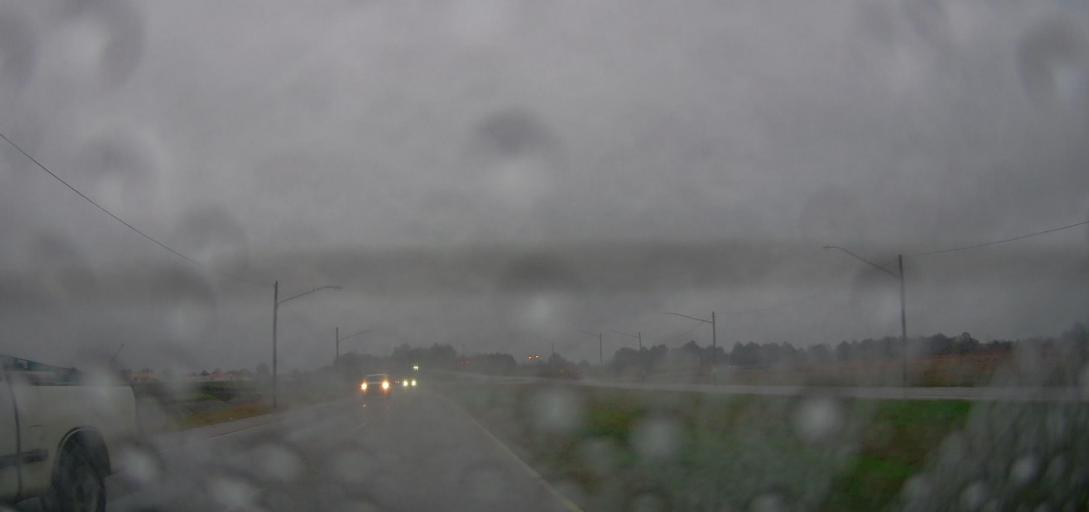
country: US
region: Alabama
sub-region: Montgomery County
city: Montgomery
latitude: 32.3681
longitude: -86.3575
